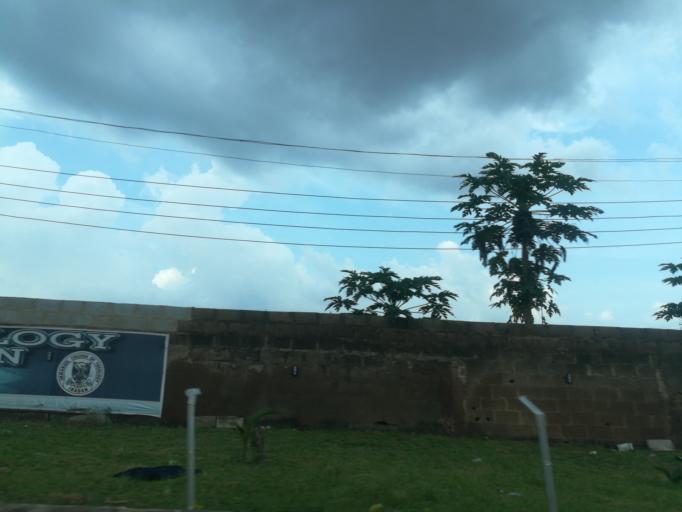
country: NG
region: Oyo
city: Ibadan
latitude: 7.4337
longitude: 3.9065
